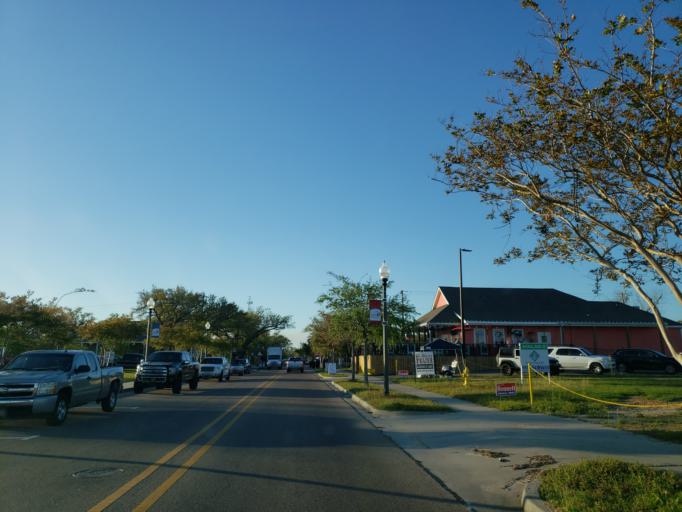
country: US
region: Mississippi
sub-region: Harrison County
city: Long Beach
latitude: 30.3461
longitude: -89.1487
